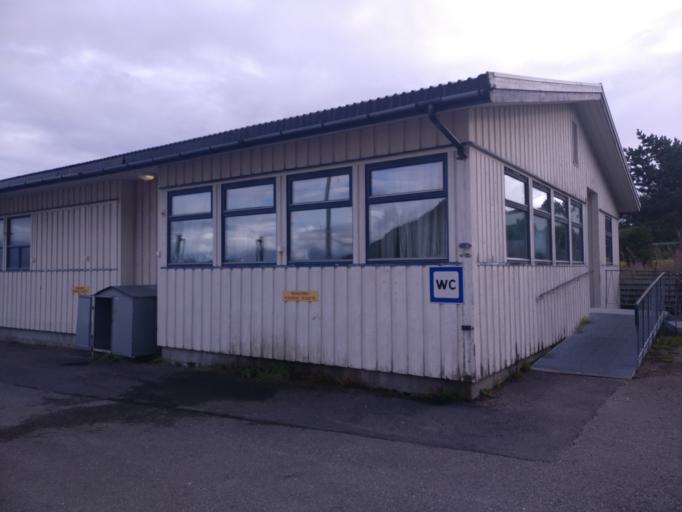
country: NO
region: Nordland
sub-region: Lodingen
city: Lodingen
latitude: 68.4198
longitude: 15.9932
